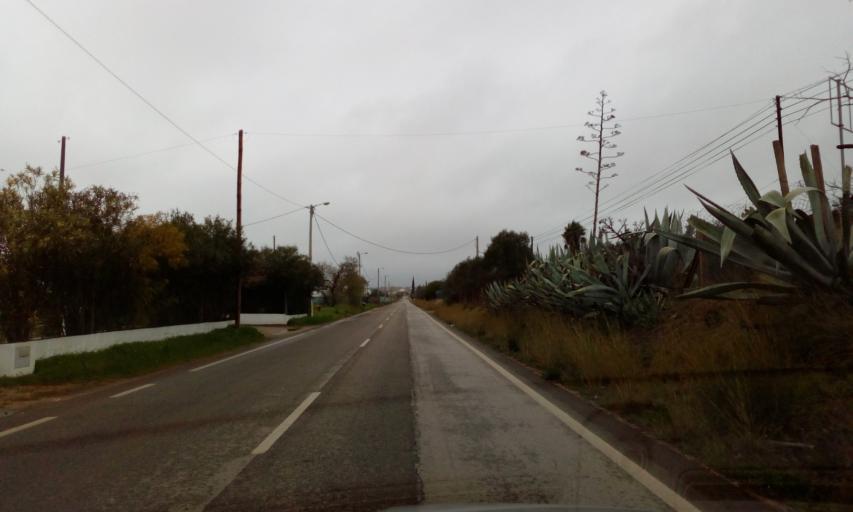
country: PT
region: Faro
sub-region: Albufeira
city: Guia
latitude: 37.1690
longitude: -8.3155
